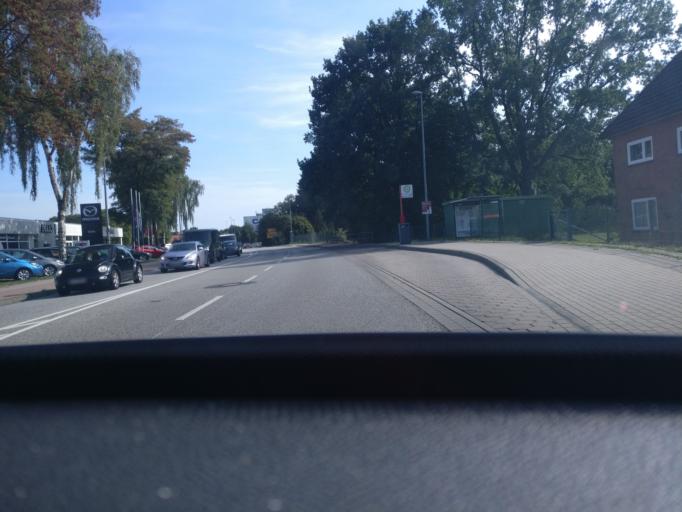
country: DE
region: Schleswig-Holstein
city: Norderstedt
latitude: 53.6671
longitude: 9.9718
